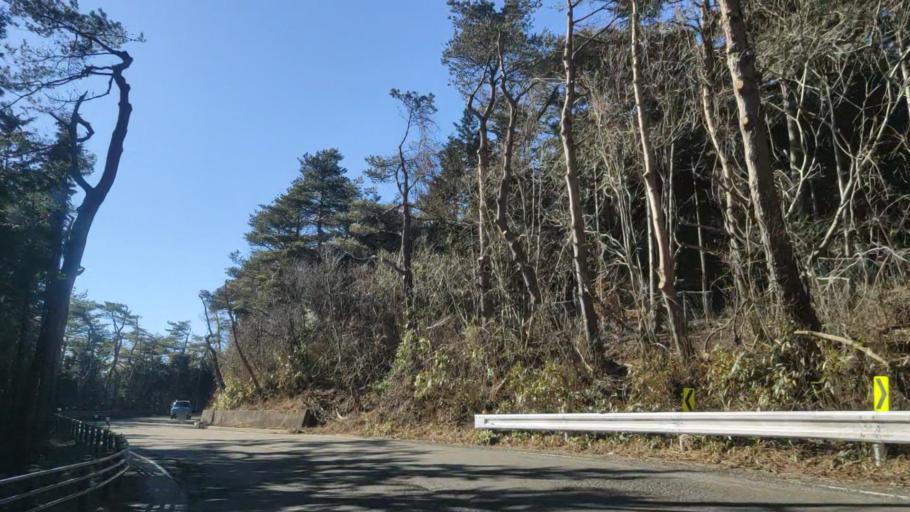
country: JP
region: Yamanashi
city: Fujikawaguchiko
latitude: 35.4381
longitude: 138.6383
